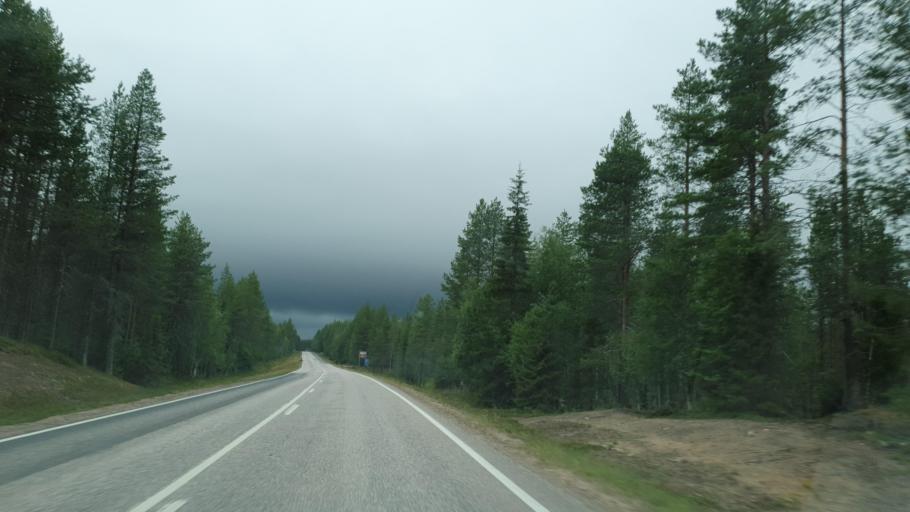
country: FI
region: Lapland
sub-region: Itae-Lappi
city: Posio
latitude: 66.5116
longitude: 28.3228
